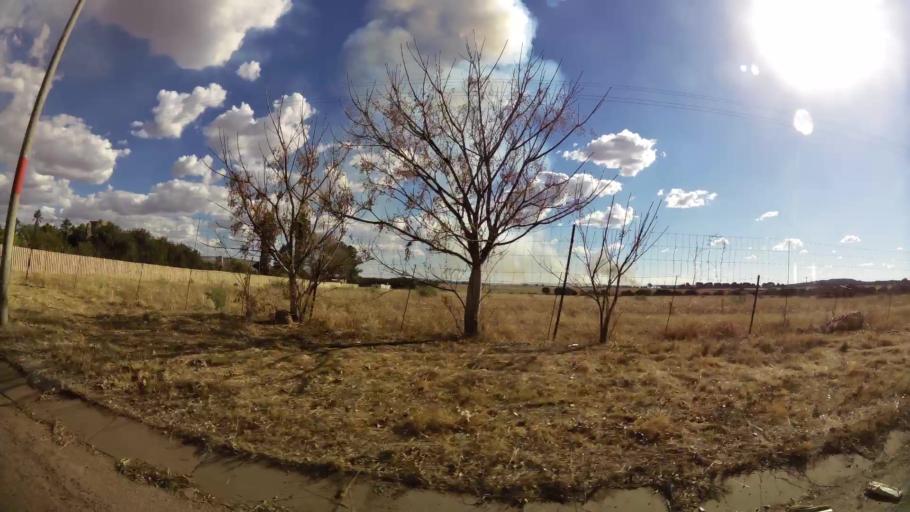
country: ZA
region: North-West
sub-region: Dr Kenneth Kaunda District Municipality
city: Klerksdorp
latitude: -26.8226
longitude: 26.6499
